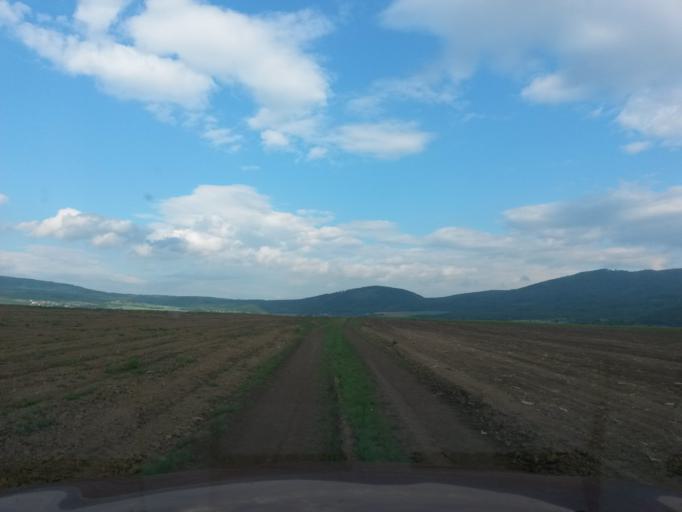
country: SK
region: Kosicky
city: Kosice
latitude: 48.7466
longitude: 21.4601
